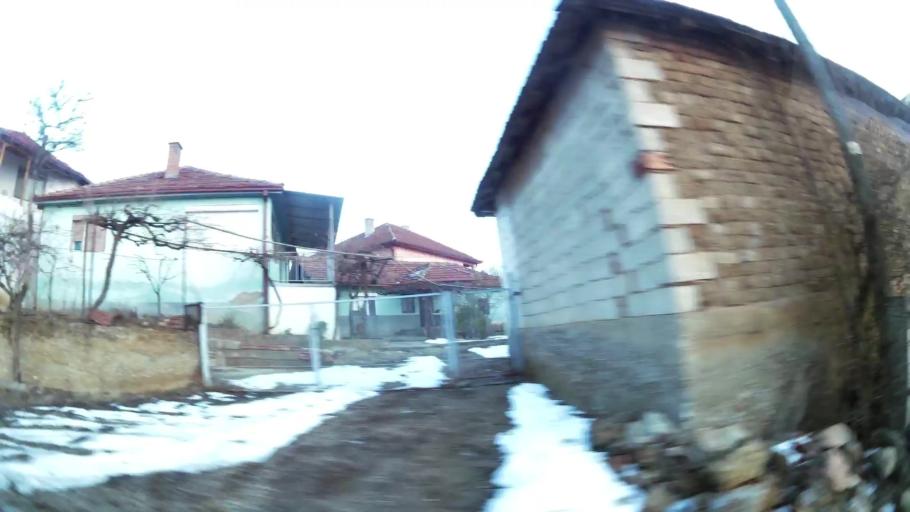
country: MK
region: Aracinovo
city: Arachinovo
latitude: 42.0339
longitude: 21.5483
